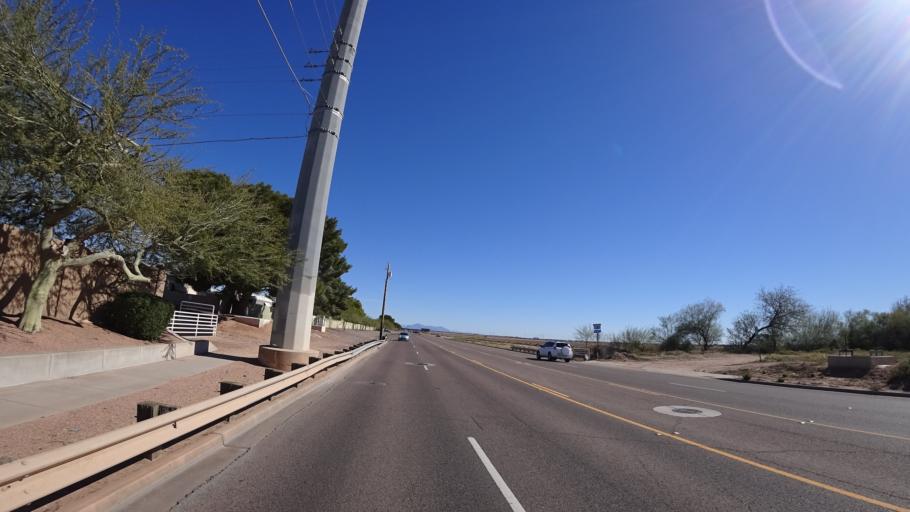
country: US
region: Arizona
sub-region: Maricopa County
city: Tempe
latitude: 33.4514
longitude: -111.9008
